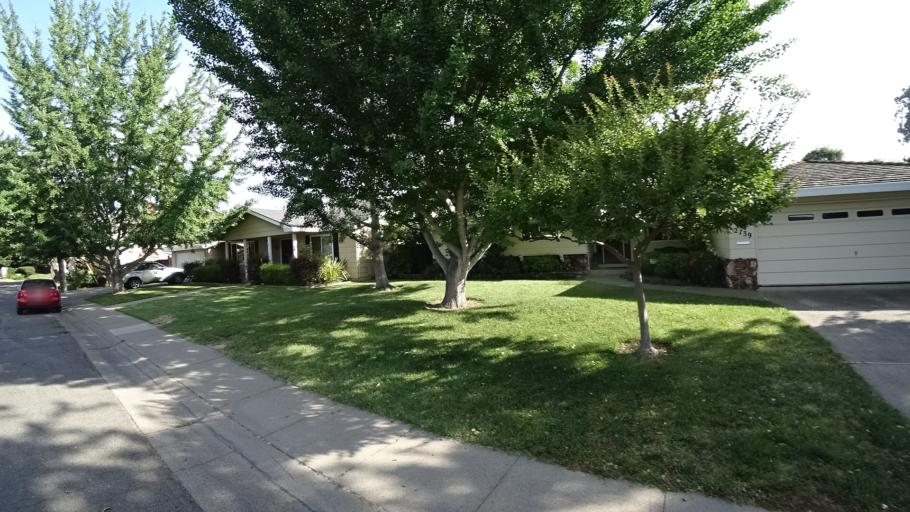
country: US
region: California
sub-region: Sacramento County
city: Rosemont
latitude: 38.5688
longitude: -121.3968
